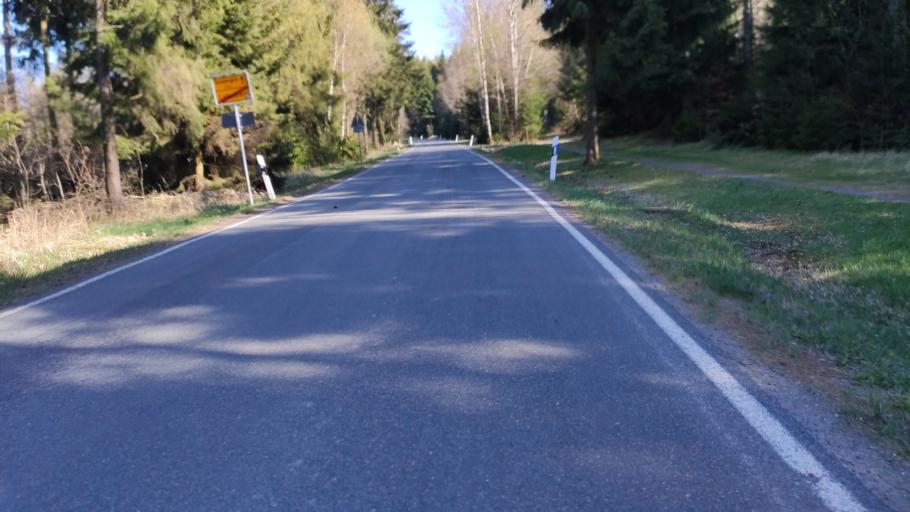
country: DE
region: Bavaria
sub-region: Upper Franconia
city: Reichenbach
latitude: 50.4687
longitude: 11.4588
